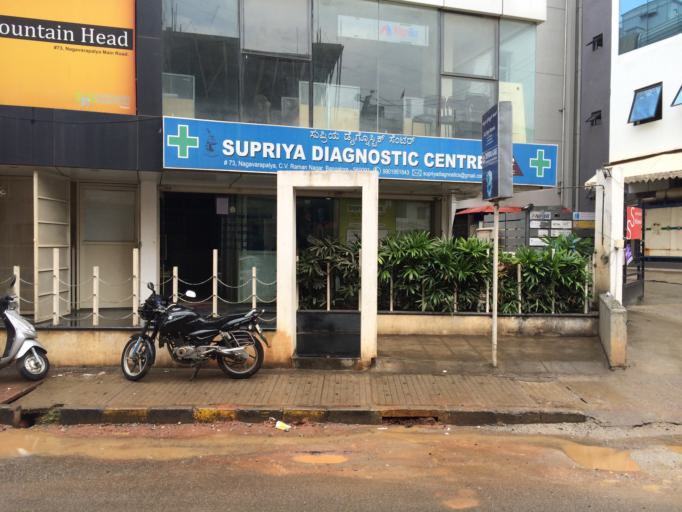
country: IN
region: Karnataka
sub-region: Bangalore Urban
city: Bangalore
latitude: 12.9896
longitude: 77.6636
